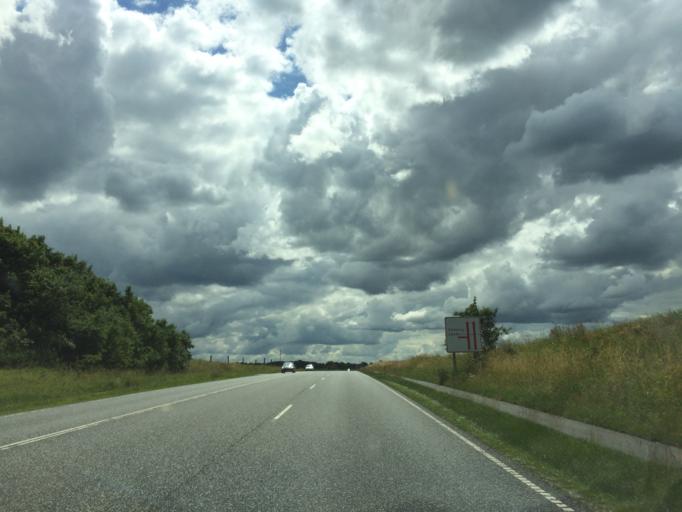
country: DK
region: Central Jutland
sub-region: Viborg Kommune
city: Viborg
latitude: 56.5468
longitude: 9.4772
